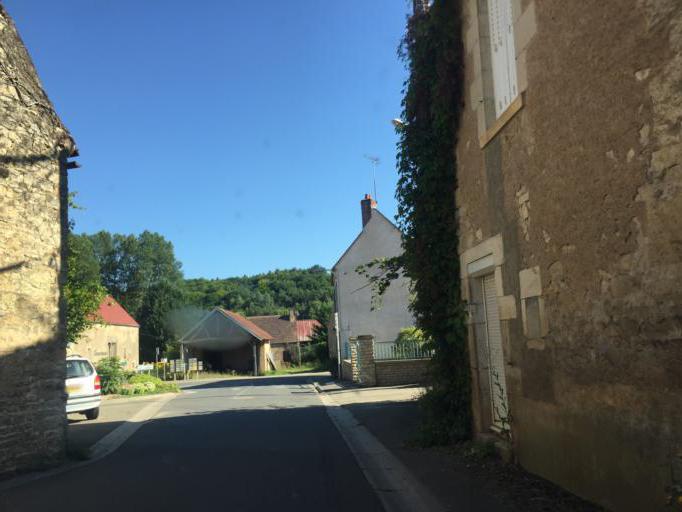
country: FR
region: Bourgogne
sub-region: Departement de l'Yonne
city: Fontenailles
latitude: 47.4795
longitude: 3.4098
